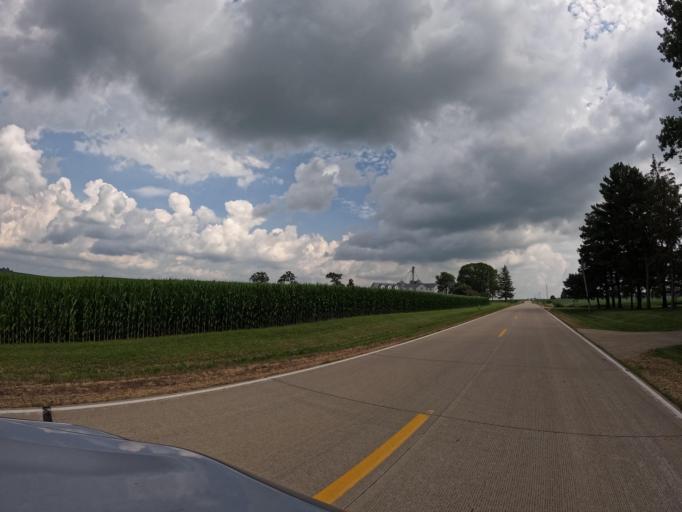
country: US
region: Iowa
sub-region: Clinton County
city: De Witt
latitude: 41.7980
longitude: -90.4132
